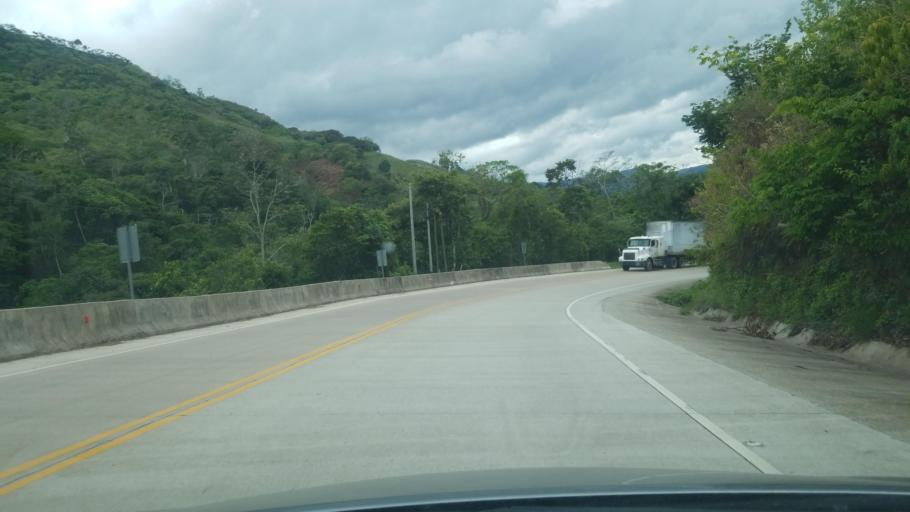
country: HN
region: Copan
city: San Jeronimo
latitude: 14.9307
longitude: -88.9556
